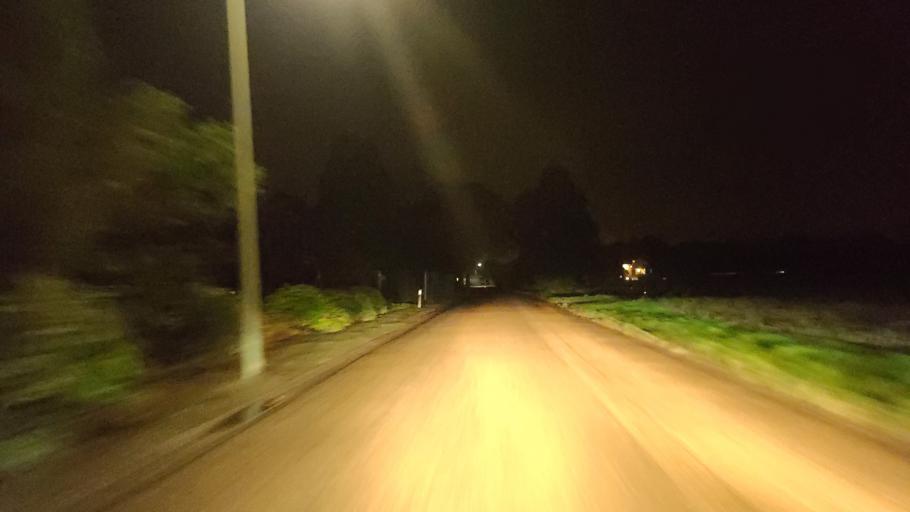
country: NL
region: Limburg
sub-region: Gemeente Gennep
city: Gennep
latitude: 51.7217
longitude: 5.9630
